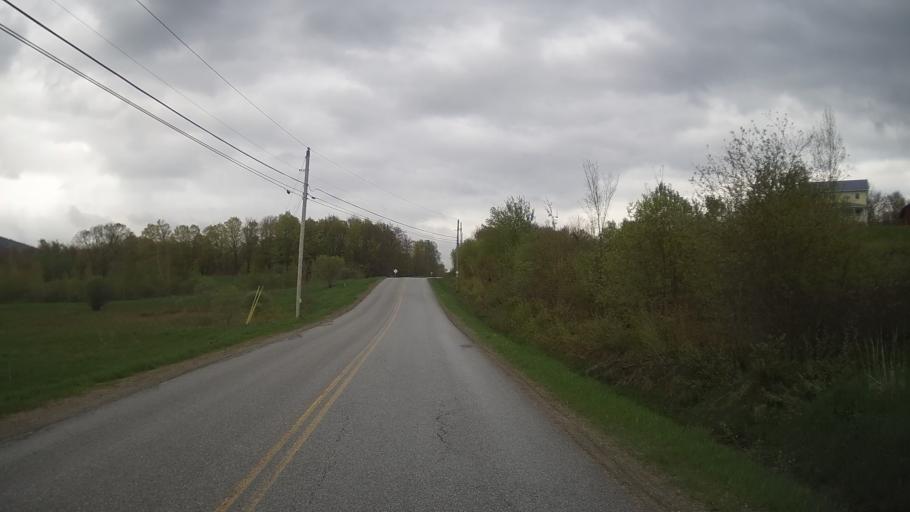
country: US
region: Vermont
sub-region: Franklin County
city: Richford
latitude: 44.9819
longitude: -72.6604
